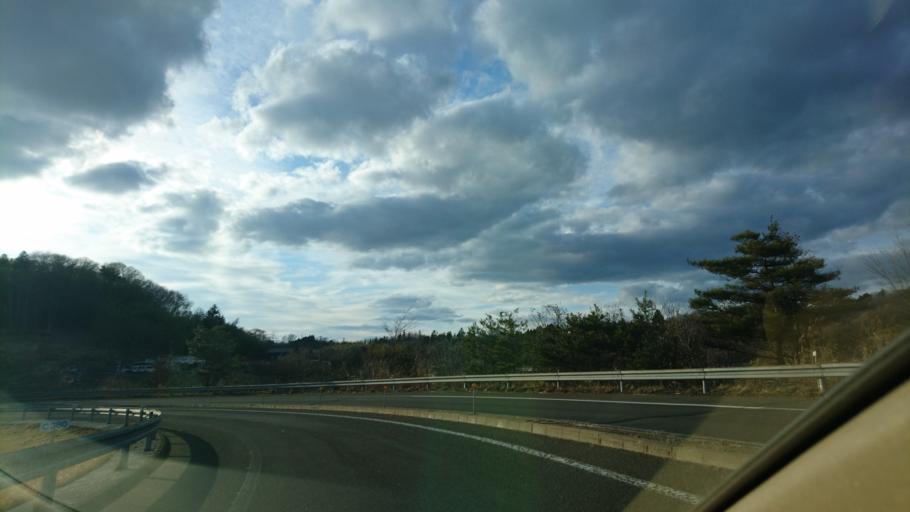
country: JP
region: Miyagi
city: Furukawa
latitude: 38.7111
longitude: 141.0087
